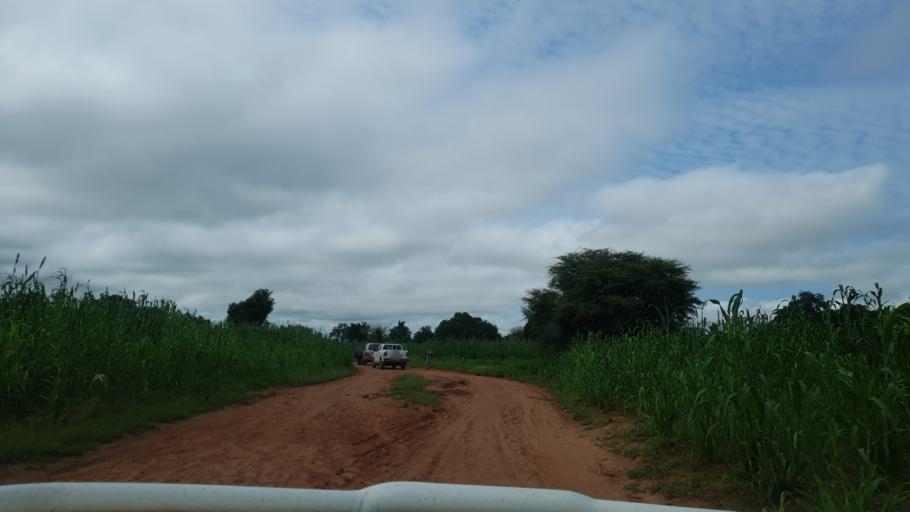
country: ML
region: Segou
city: Baroueli
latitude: 13.5024
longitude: -6.8982
